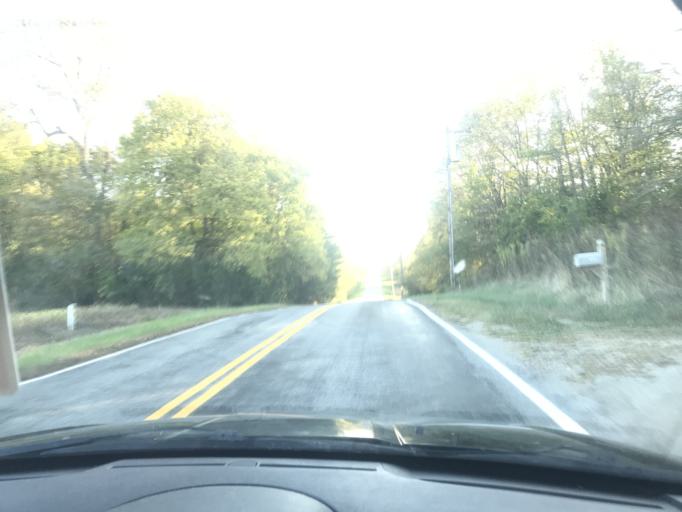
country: US
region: Ohio
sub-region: Logan County
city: De Graff
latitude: 40.2375
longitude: -83.8629
